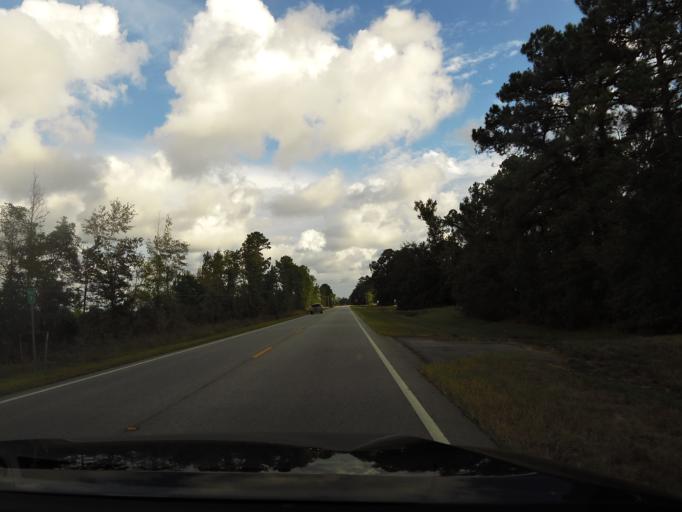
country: US
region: Georgia
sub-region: Liberty County
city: Midway
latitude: 31.7629
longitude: -81.4470
